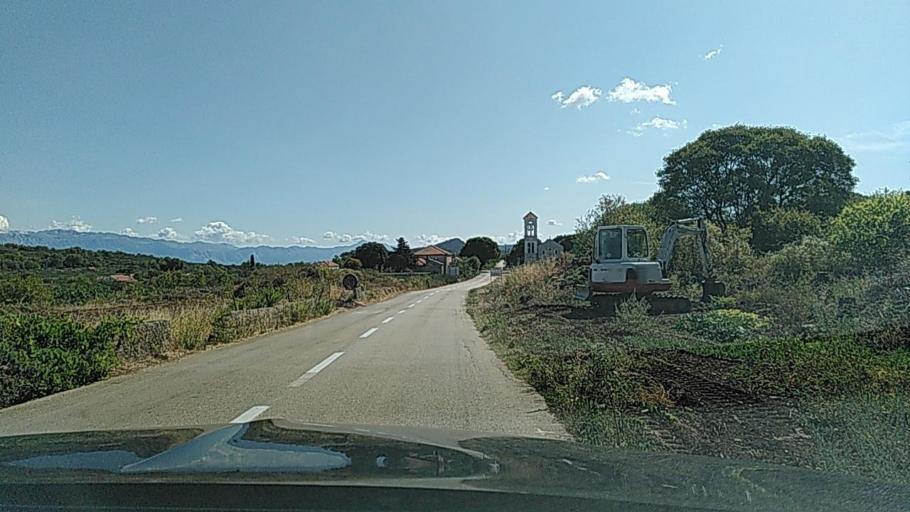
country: HR
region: Splitsko-Dalmatinska
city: Jelsa
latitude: 43.1491
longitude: 16.7911
